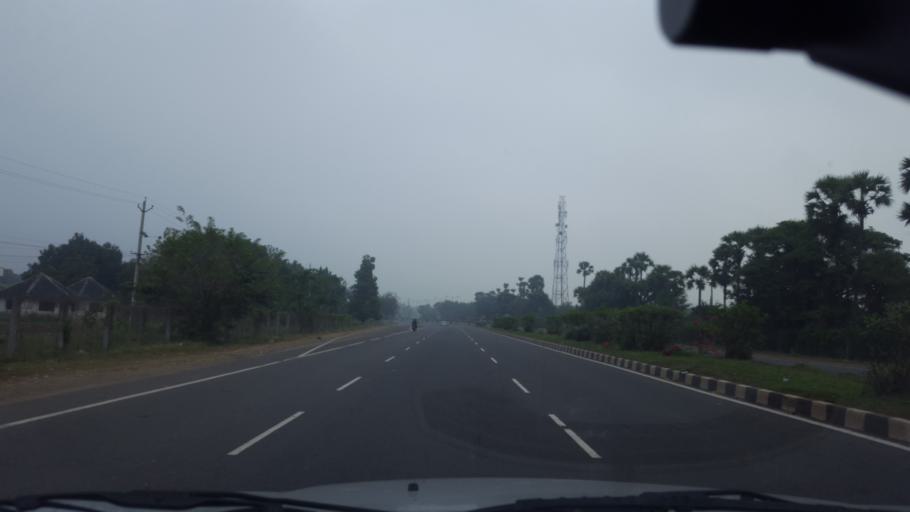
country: IN
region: Andhra Pradesh
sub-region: Prakasam
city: Addanki
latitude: 15.8358
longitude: 80.0485
